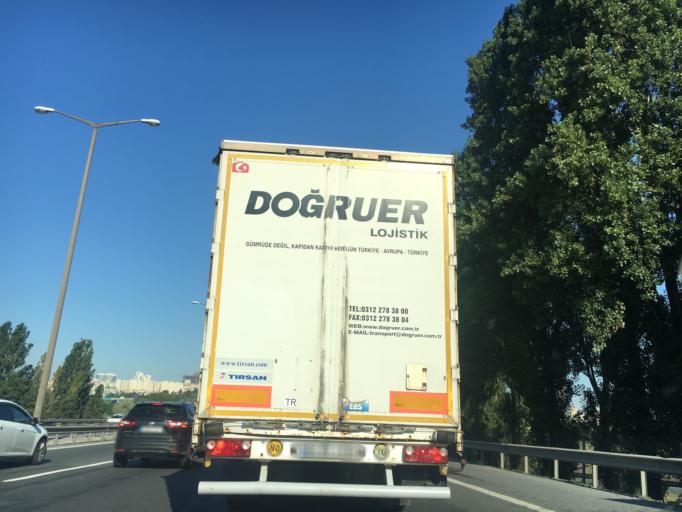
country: TR
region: Istanbul
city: Esenyurt
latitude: 41.0589
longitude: 28.7041
